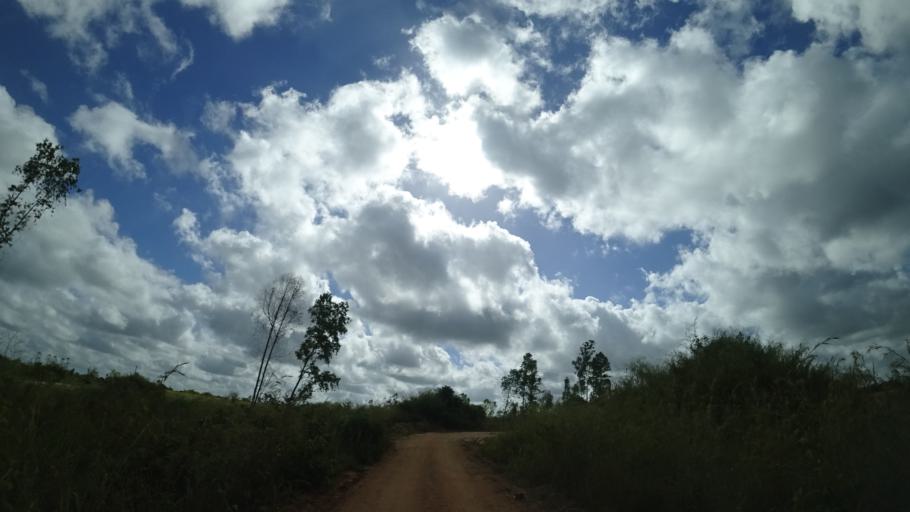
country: MZ
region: Sofala
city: Dondo
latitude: -19.4245
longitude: 34.7082
